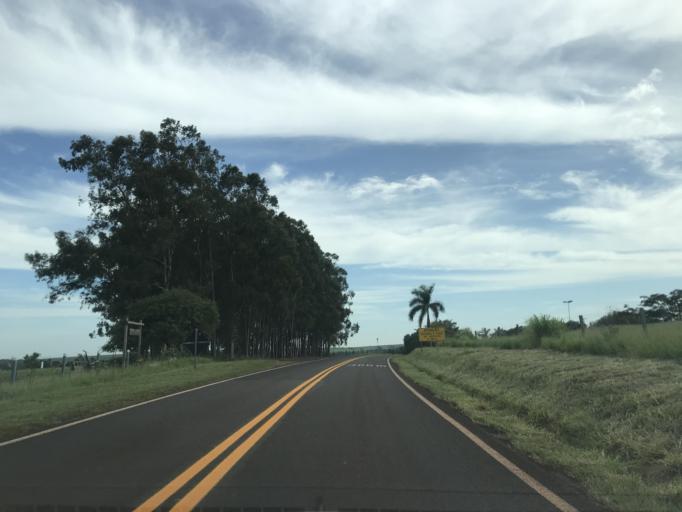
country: BR
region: Parana
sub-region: Terra Rica
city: Terra Rica
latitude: -22.7802
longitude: -52.6572
